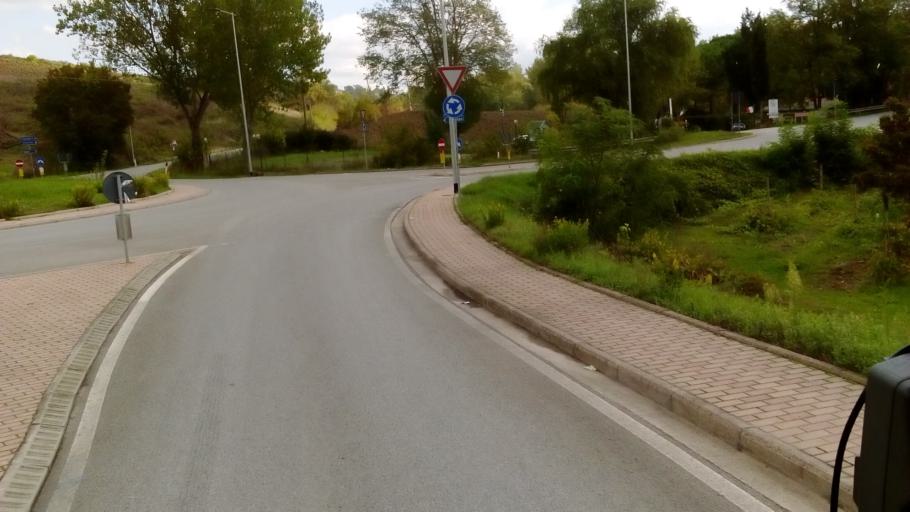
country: IT
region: Tuscany
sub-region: Province of Florence
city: Montespertoli
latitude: 43.6612
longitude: 11.0841
